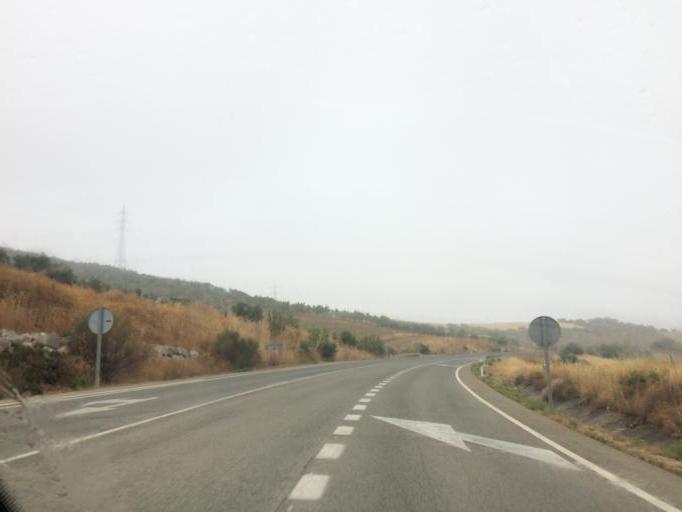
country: ES
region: Andalusia
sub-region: Provincia de Malaga
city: Casabermeja
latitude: 36.9038
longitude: -4.4386
